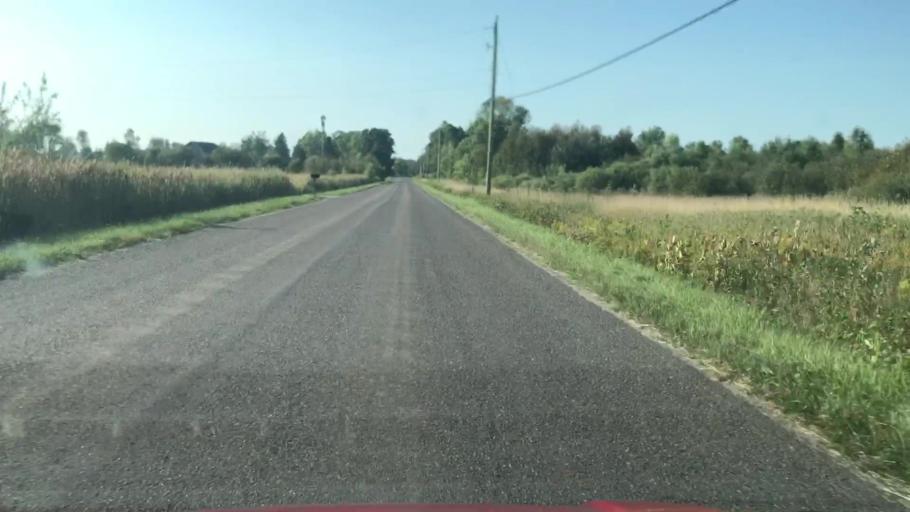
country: US
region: Michigan
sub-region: Chippewa County
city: Sault Ste. Marie
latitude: 46.2869
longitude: -84.0583
